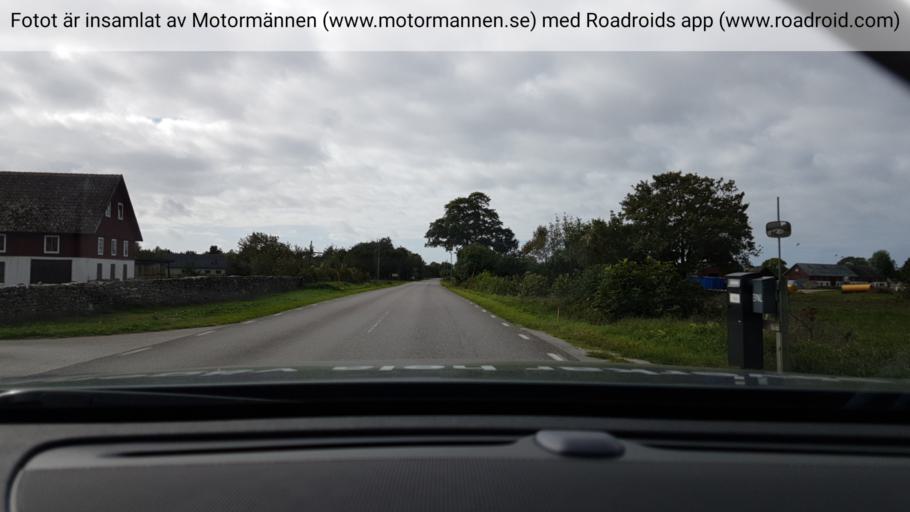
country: SE
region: Gotland
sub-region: Gotland
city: Hemse
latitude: 56.9675
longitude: 18.2292
